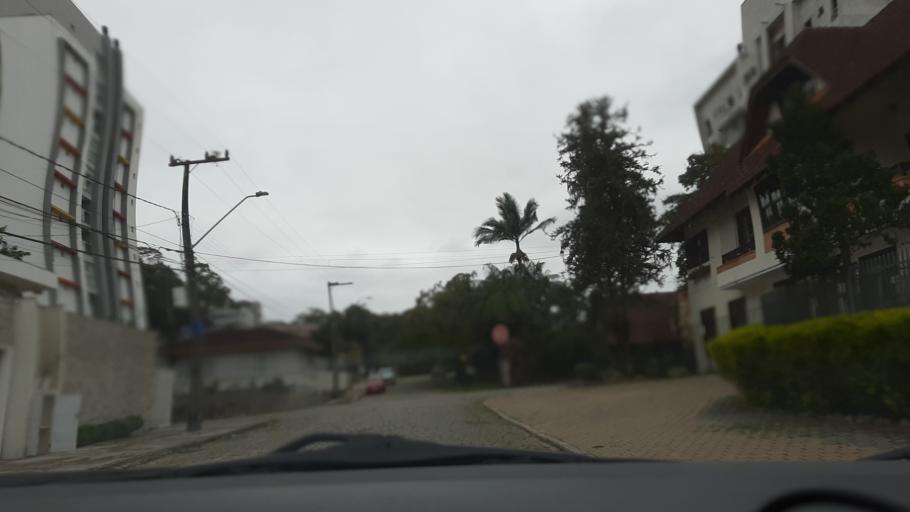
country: BR
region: Santa Catarina
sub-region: Joinville
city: Joinville
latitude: -26.3142
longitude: -48.8560
